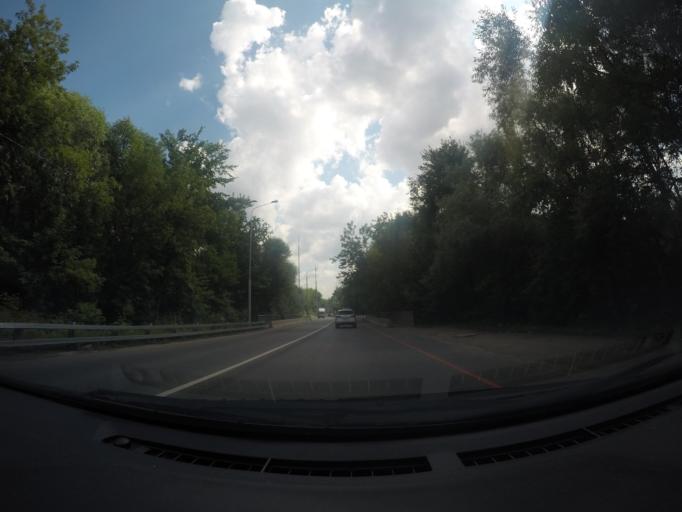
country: RU
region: Moscow
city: Sviblovo
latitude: 55.8441
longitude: 37.6270
